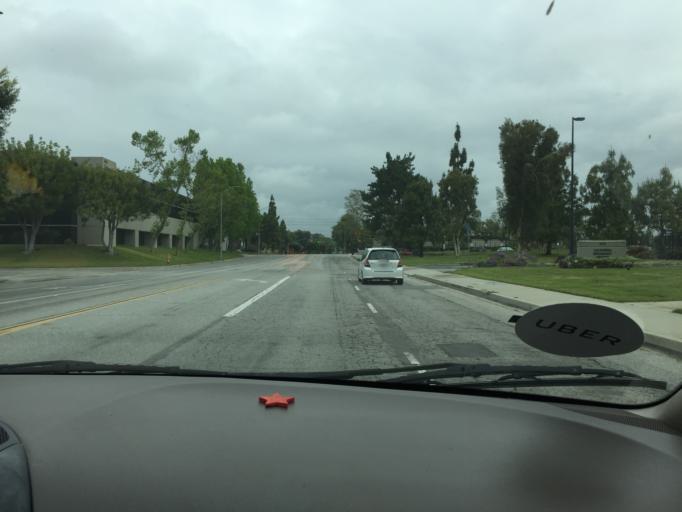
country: US
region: California
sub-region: Los Angeles County
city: Signal Hill
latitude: 33.8294
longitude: -118.2125
